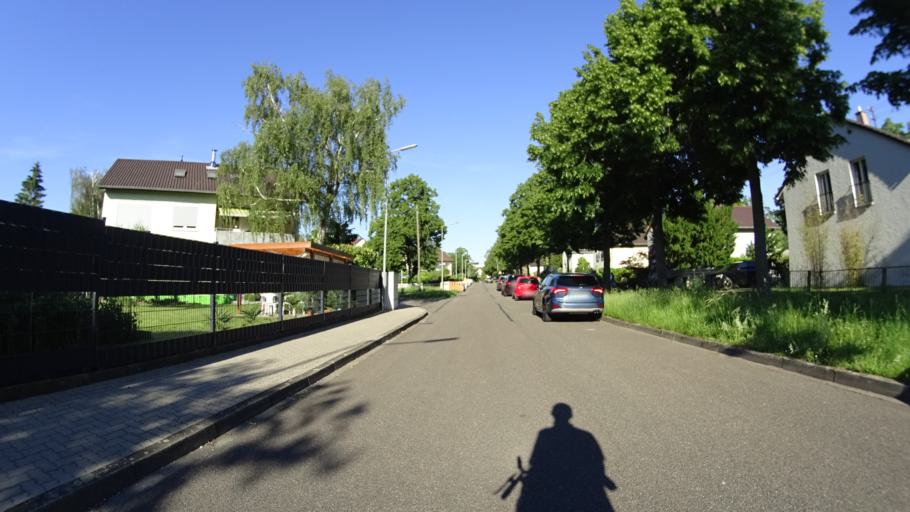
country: DE
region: Baden-Wuerttemberg
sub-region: Karlsruhe Region
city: Karlsruhe
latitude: 49.0349
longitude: 8.3662
